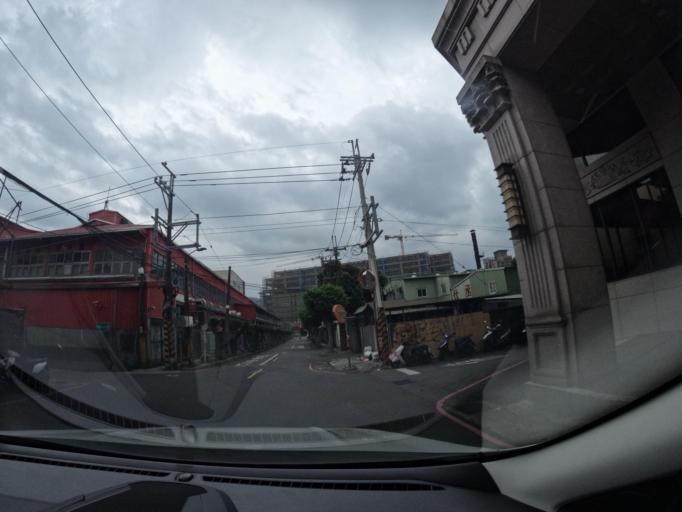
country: TW
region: Taipei
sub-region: Taipei
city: Banqiao
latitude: 24.9644
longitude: 121.4210
